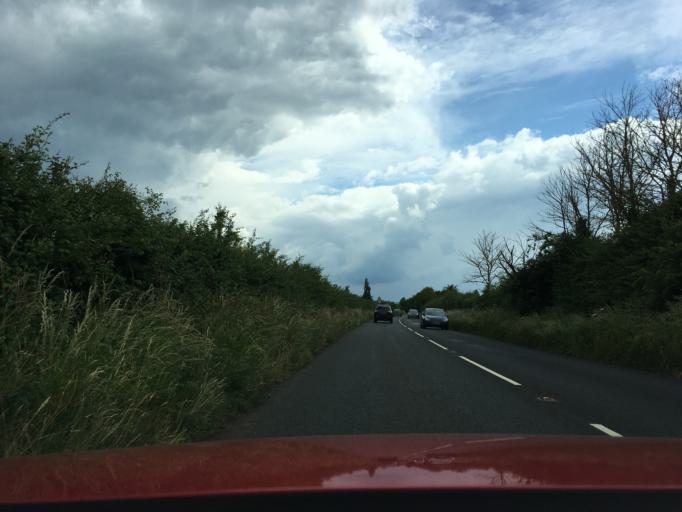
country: GB
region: England
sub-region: Gloucestershire
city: Stonehouse
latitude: 51.7847
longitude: -2.2896
